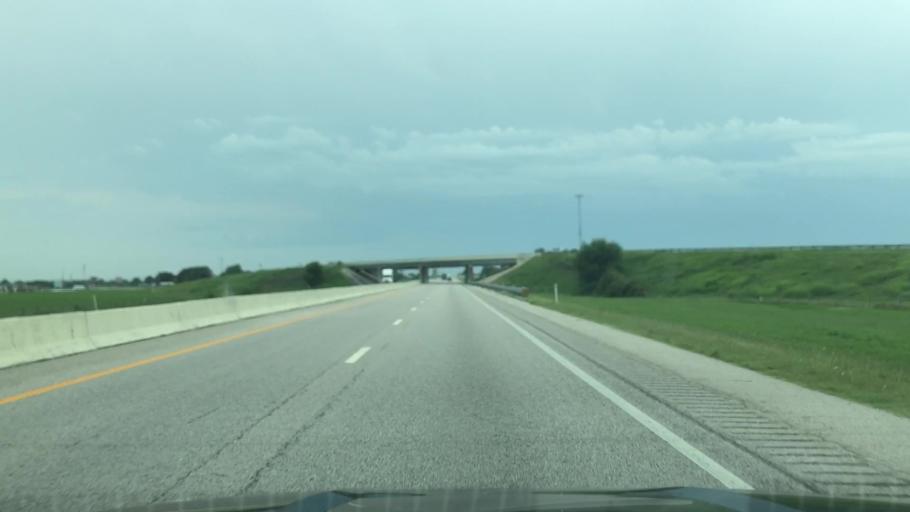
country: US
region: Oklahoma
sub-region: Craig County
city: Vinita
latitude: 36.5601
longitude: -95.2188
